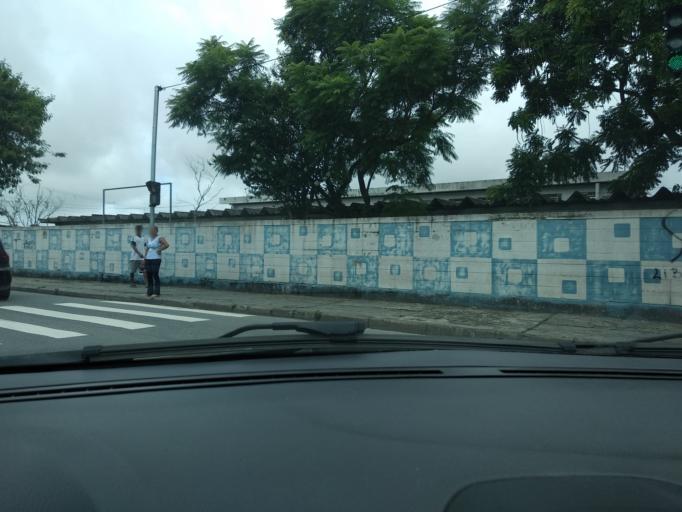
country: BR
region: Sao Paulo
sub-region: Mogi das Cruzes
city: Mogi das Cruzes
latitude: -23.5382
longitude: -46.1825
